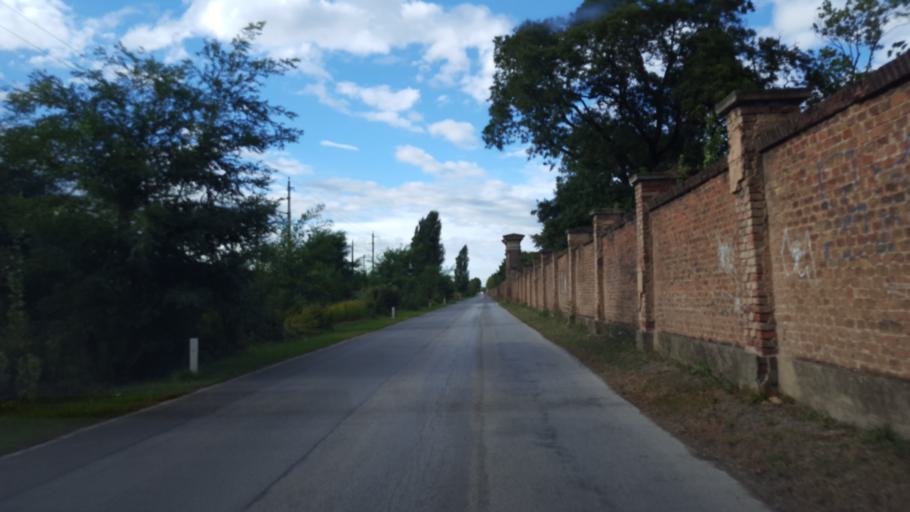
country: AT
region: Lower Austria
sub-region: Politischer Bezirk Wien-Umgebung
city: Schwechat
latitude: 48.1445
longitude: 16.4324
